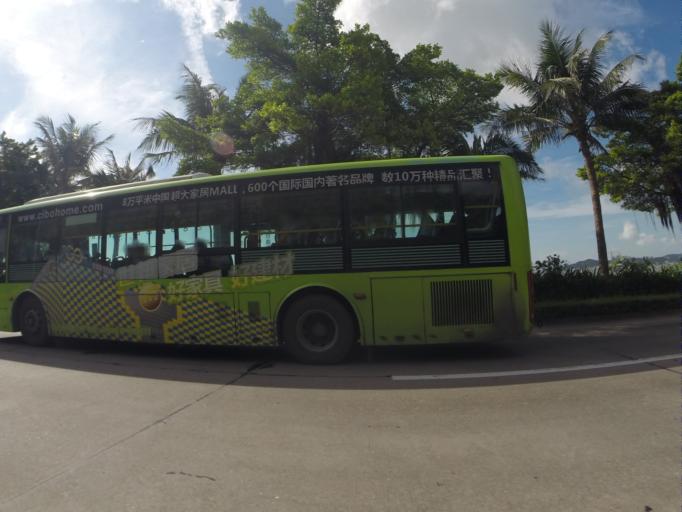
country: CN
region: Guangdong
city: Zhuhai
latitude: 22.3132
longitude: 113.5807
